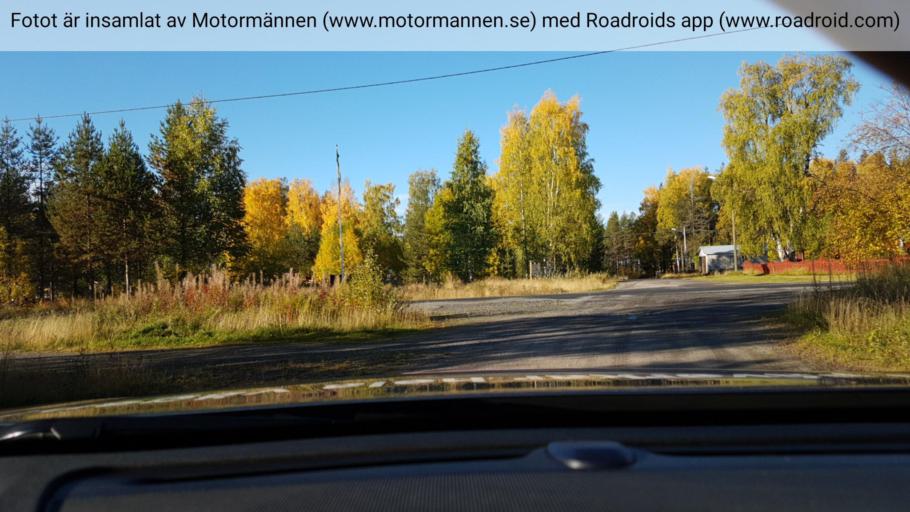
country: SE
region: Norrbotten
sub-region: Alvsbyns Kommun
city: AElvsbyn
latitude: 66.2761
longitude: 21.1239
